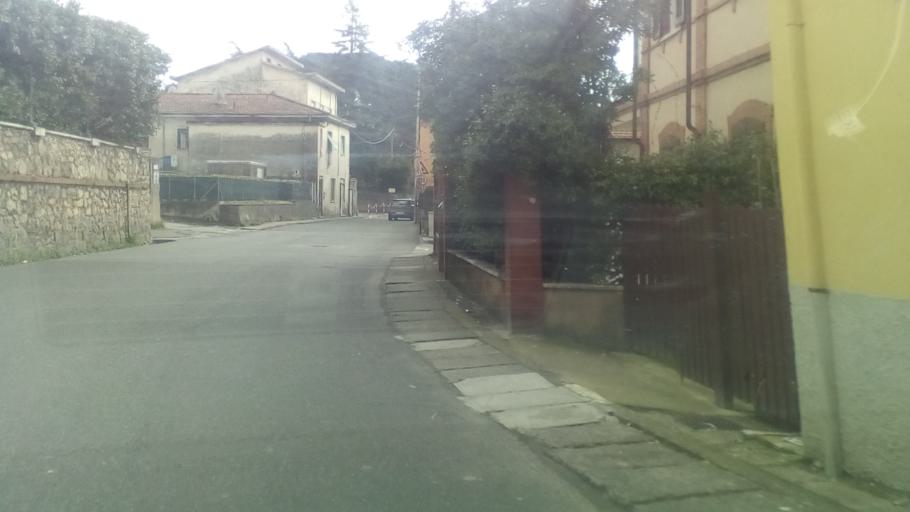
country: IT
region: Tuscany
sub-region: Provincia di Massa-Carrara
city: Carrara
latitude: 44.0649
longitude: 10.0837
